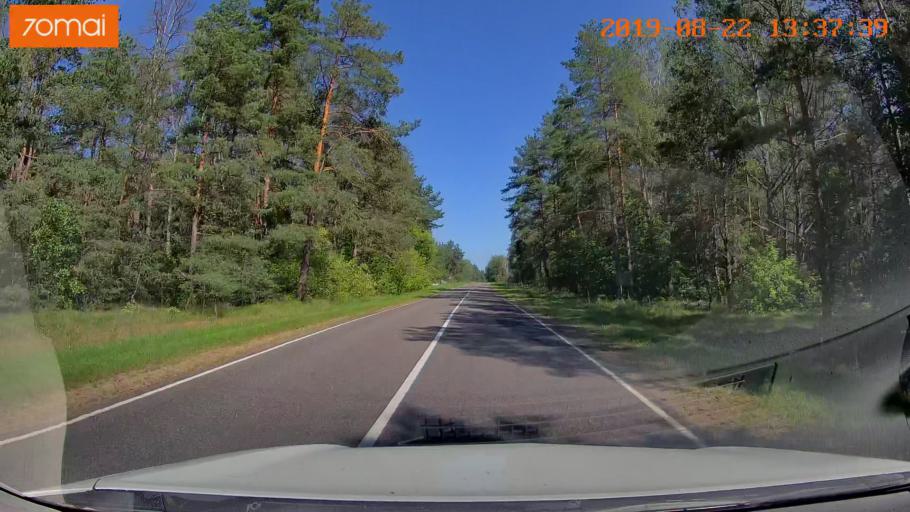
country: BY
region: Minsk
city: Staryya Darohi
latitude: 53.2167
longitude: 28.3037
